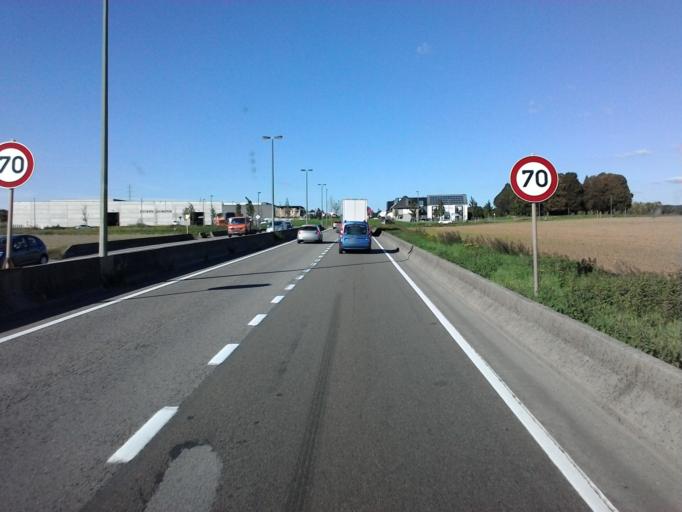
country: BE
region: Wallonia
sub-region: Province du Luxembourg
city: Messancy
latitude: 49.6342
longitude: 5.8138
